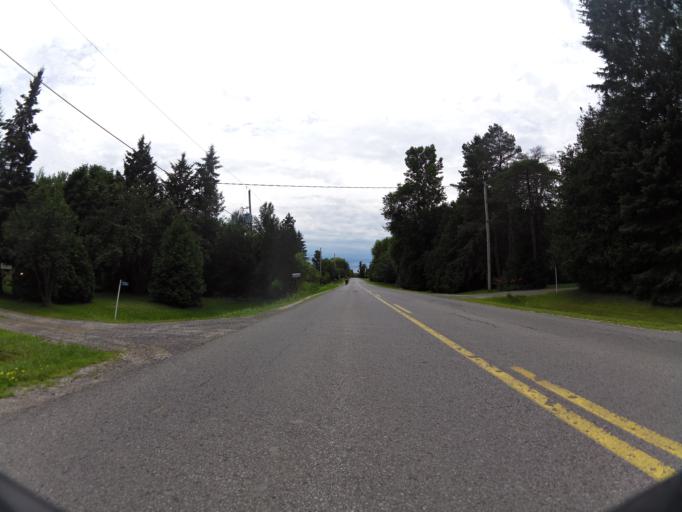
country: CA
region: Ontario
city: Prescott
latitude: 45.0351
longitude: -75.6211
